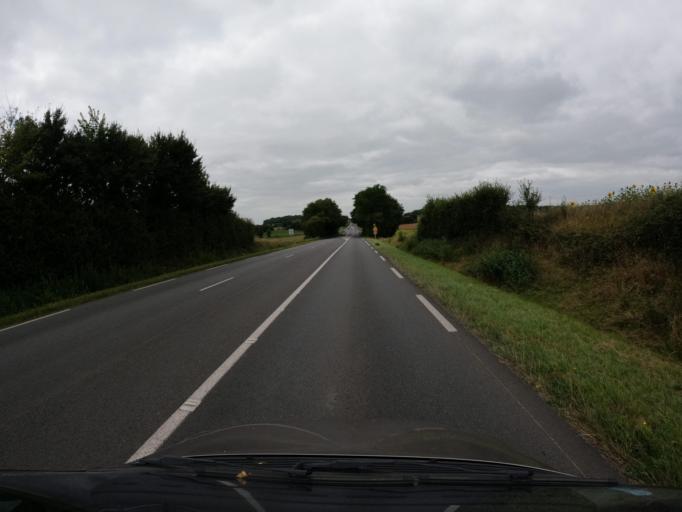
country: FR
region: Poitou-Charentes
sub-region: Departement des Deux-Sevres
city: Celles-sur-Belle
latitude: 46.2447
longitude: -0.1844
